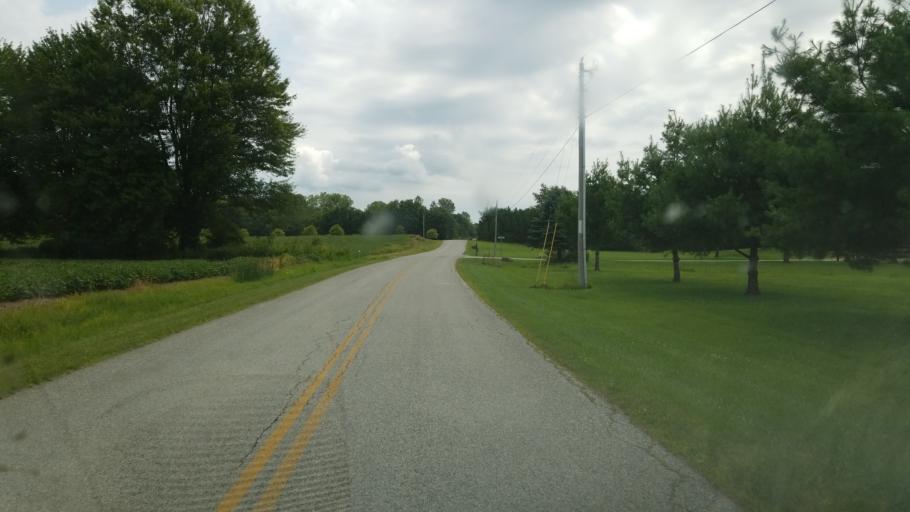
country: US
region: Ohio
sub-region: Knox County
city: Centerburg
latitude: 40.3249
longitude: -82.7867
